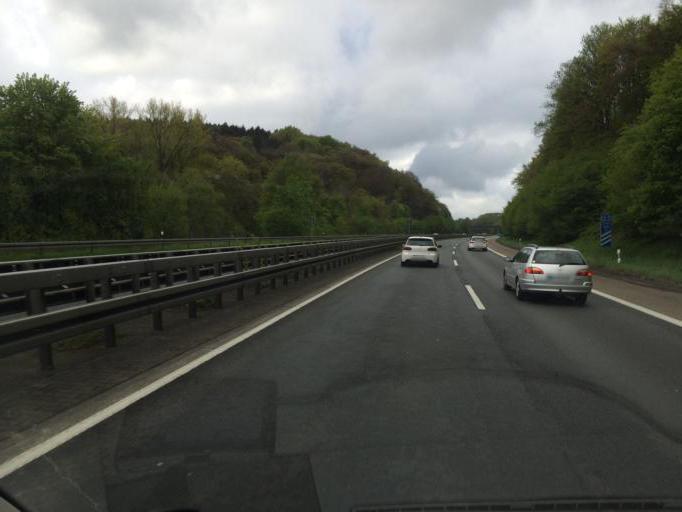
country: DE
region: North Rhine-Westphalia
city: Sprockhovel
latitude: 51.3626
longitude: 7.2757
